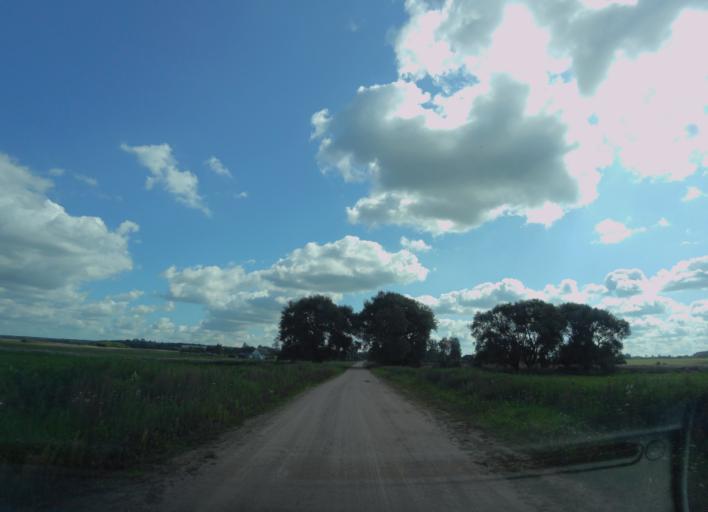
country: BY
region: Minsk
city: Zyembin
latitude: 54.3780
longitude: 28.3630
